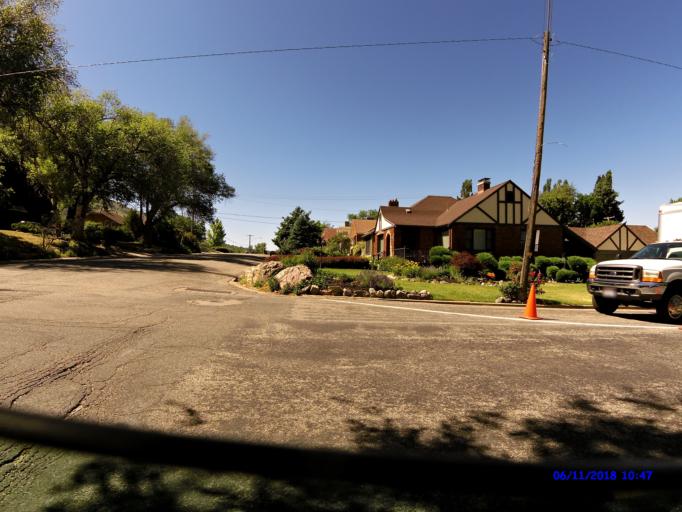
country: US
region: Utah
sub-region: Weber County
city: Ogden
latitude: 41.2119
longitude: -111.9402
